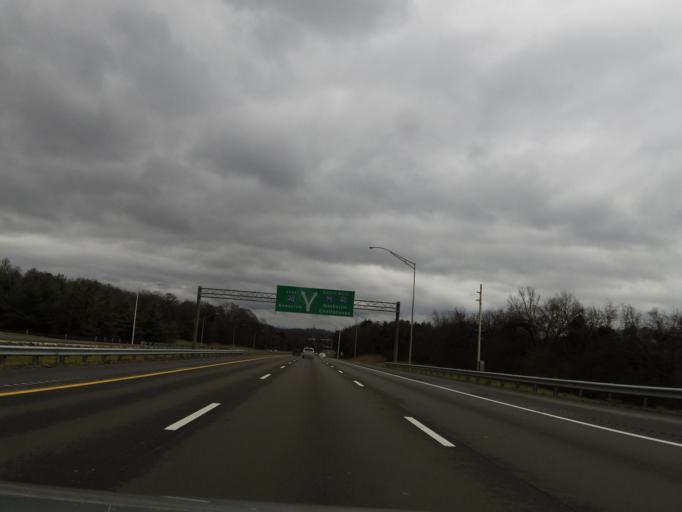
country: US
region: Tennessee
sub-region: Knox County
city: Knoxville
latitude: 35.9675
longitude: -83.9791
